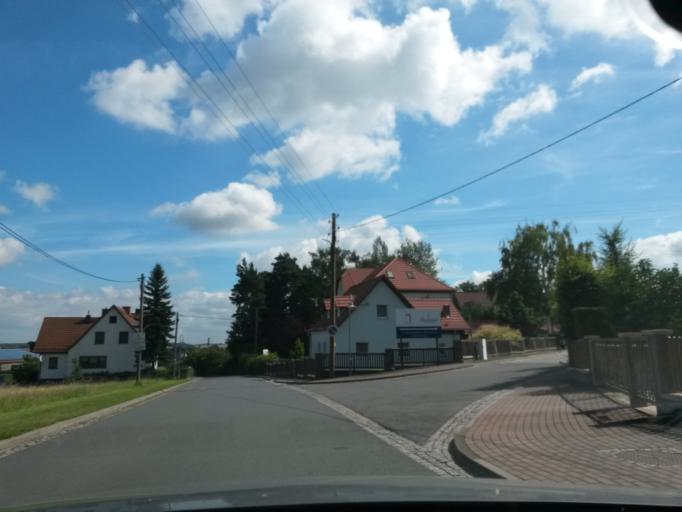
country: DE
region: Thuringia
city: Reichenbach
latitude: 50.8637
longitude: 11.8707
